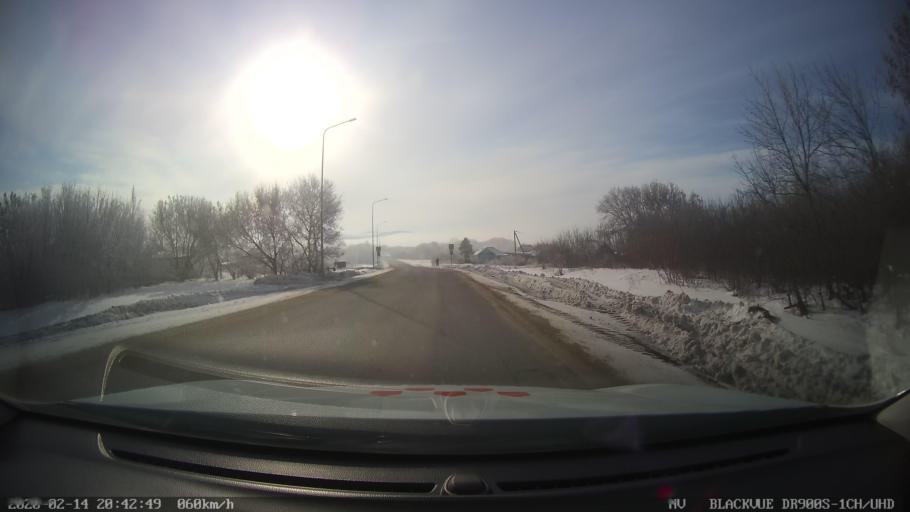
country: RU
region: Tatarstan
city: Kuybyshevskiy Zaton
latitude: 55.3140
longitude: 49.1445
